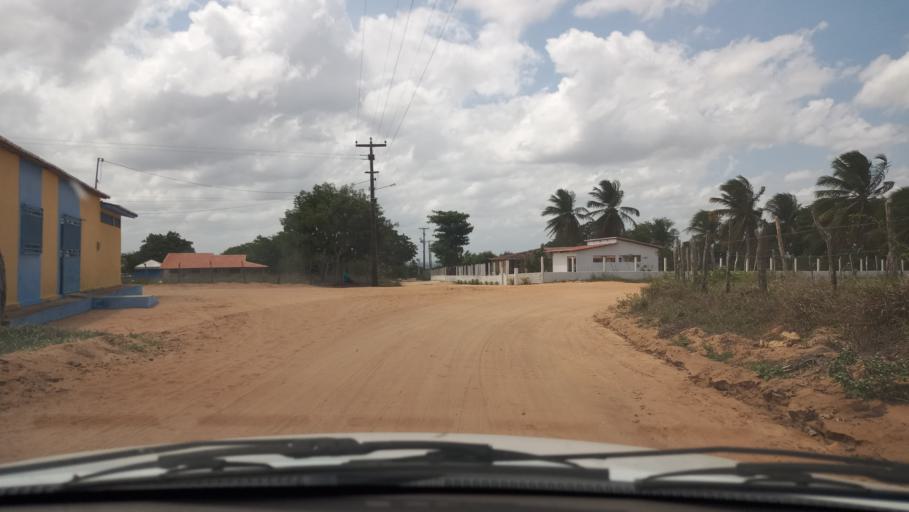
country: BR
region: Rio Grande do Norte
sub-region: Montanhas
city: Montanhas
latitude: -6.3580
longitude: -35.3376
